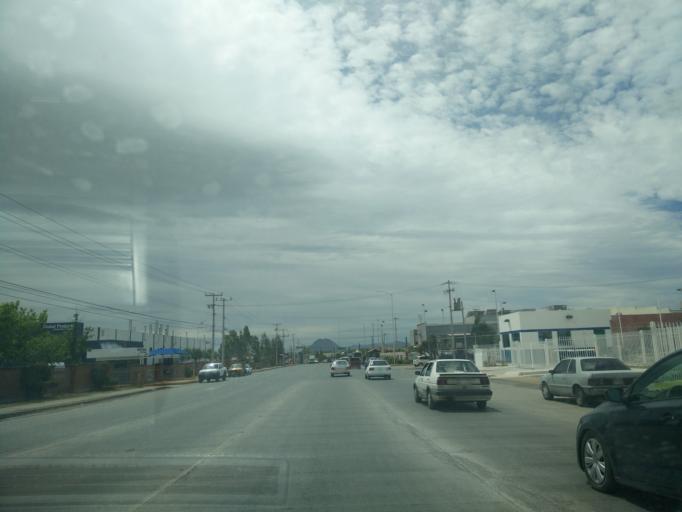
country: MX
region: Chihuahua
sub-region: Chihuahua
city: Chihuahua
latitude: 28.7115
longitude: -106.1139
